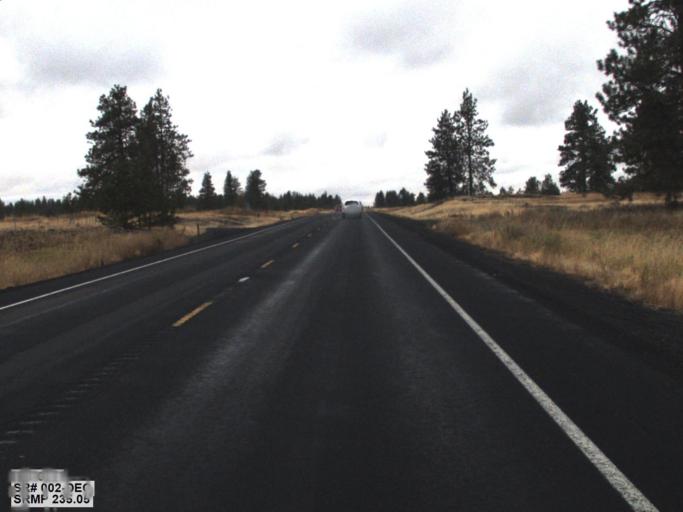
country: US
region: Washington
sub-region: Lincoln County
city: Davenport
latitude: 47.7216
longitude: -118.4467
